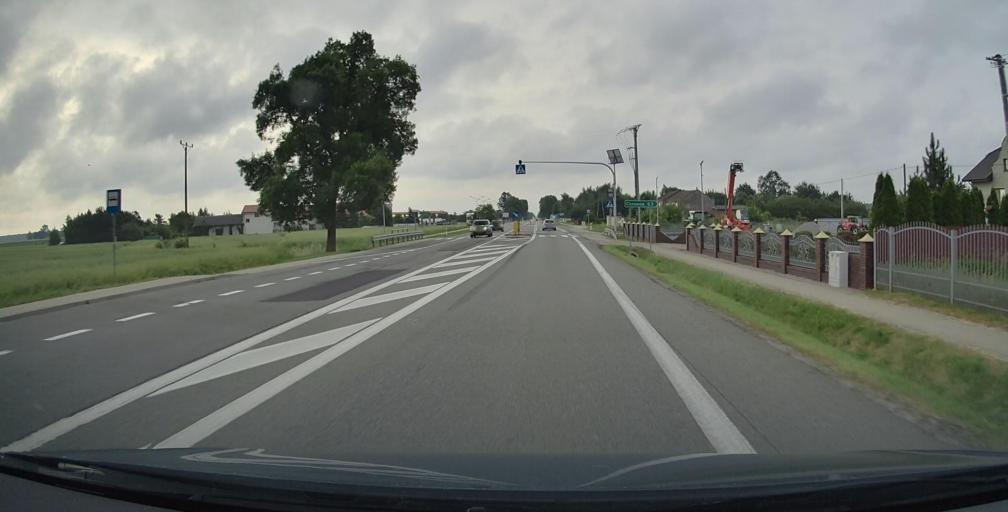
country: PL
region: Masovian Voivodeship
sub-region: Powiat siedlecki
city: Zbuczyn
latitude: 52.1089
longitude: 22.3847
